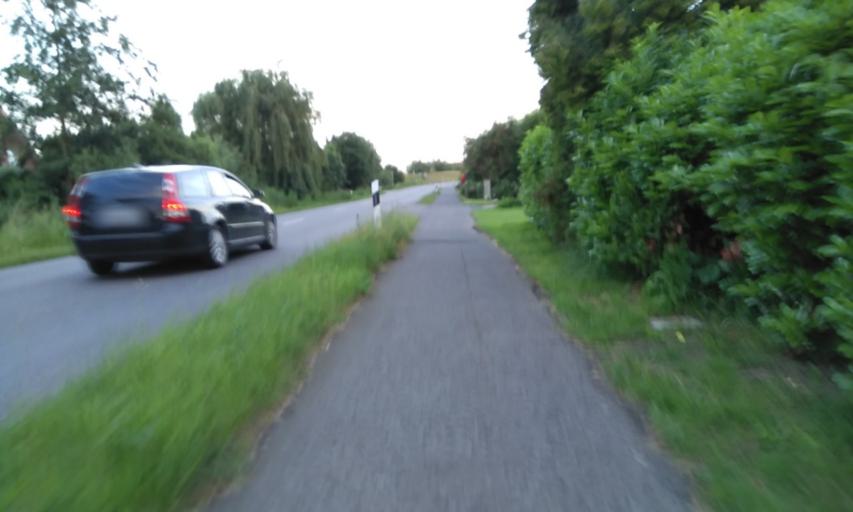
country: DE
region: Lower Saxony
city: Jork
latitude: 53.5035
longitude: 9.7277
